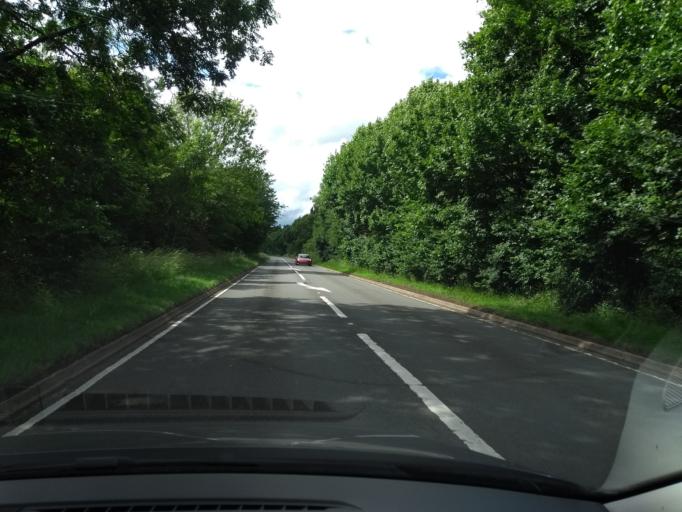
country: GB
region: England
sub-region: Warwickshire
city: Henley in Arden
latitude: 52.2854
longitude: -1.7403
